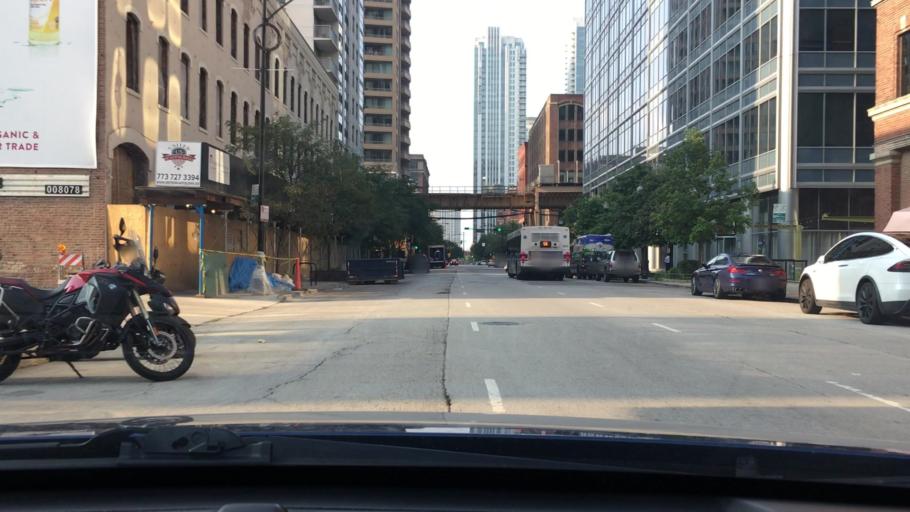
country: US
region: Illinois
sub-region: Cook County
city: Chicago
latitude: 41.8845
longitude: -87.6428
